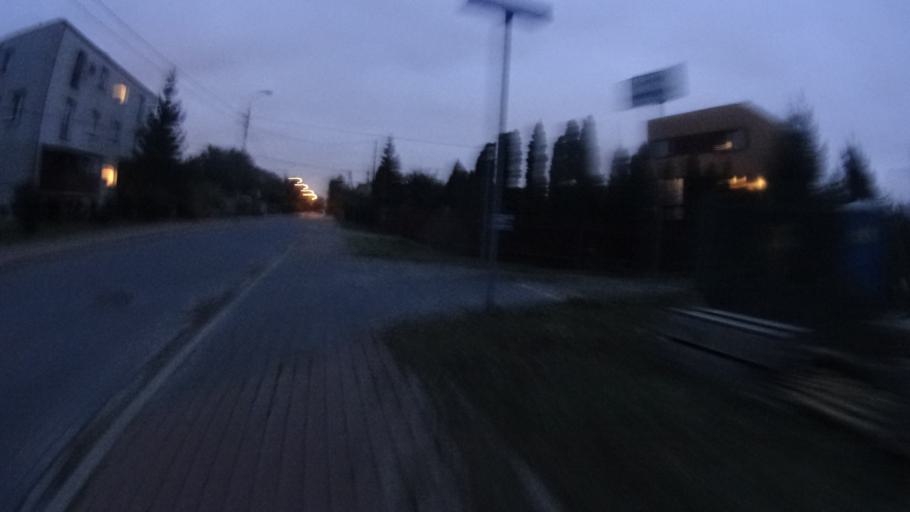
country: PL
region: Masovian Voivodeship
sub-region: Powiat warszawski zachodni
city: Babice
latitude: 52.2280
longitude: 20.8622
